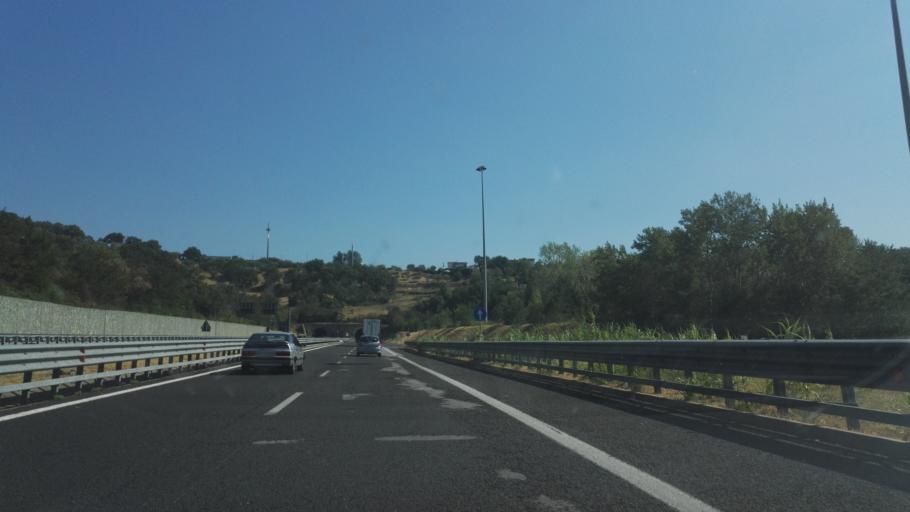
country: IT
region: Calabria
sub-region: Provincia di Cosenza
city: Rosario
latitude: 39.2993
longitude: 16.2362
